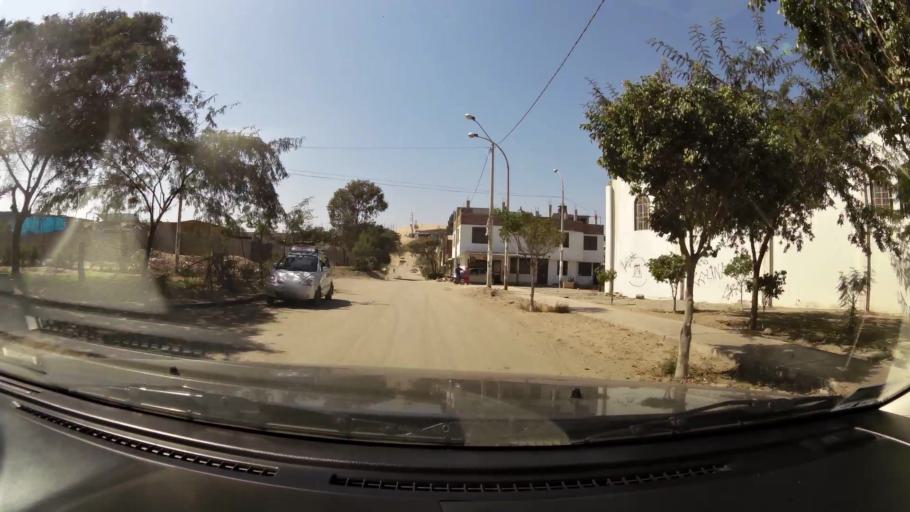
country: PE
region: Ica
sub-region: Provincia de Ica
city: Subtanjalla
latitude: -14.0374
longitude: -75.7497
